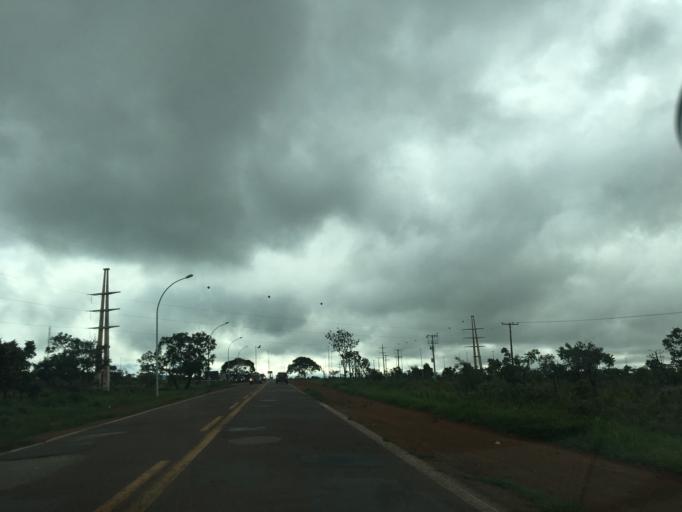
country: BR
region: Federal District
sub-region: Brasilia
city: Brasilia
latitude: -15.9763
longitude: -47.9870
